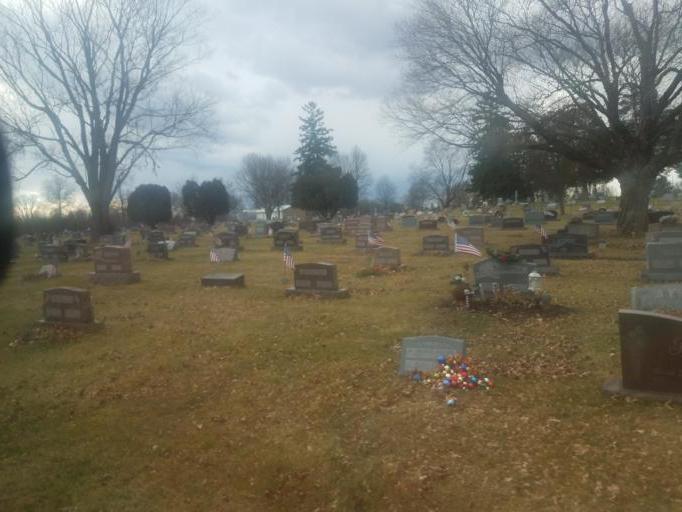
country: US
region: Ohio
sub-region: Marion County
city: Prospect
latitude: 40.4576
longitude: -83.0796
